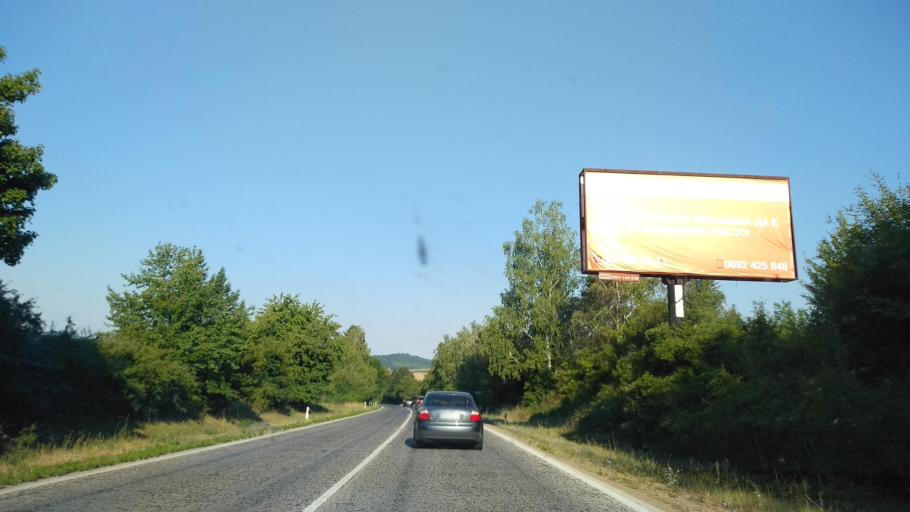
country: BG
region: Lovech
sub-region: Obshtina Lovech
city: Lovech
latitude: 43.0508
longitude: 24.9054
